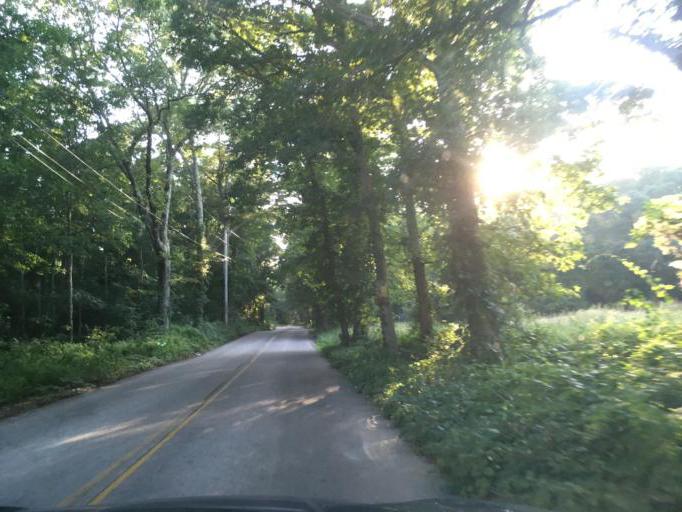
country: US
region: Rhode Island
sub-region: Kent County
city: West Warwick
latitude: 41.6464
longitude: -71.5476
